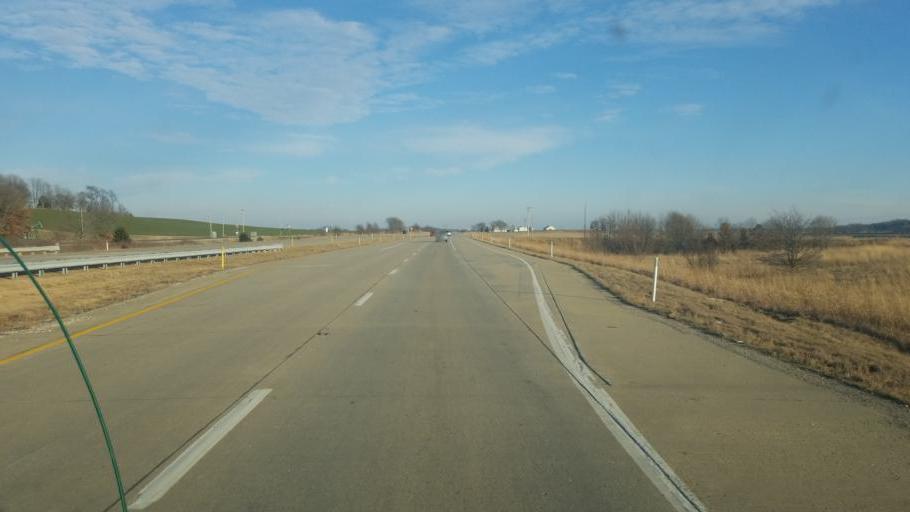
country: US
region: Indiana
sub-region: Knox County
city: Bicknell
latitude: 38.6754
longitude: -87.3713
